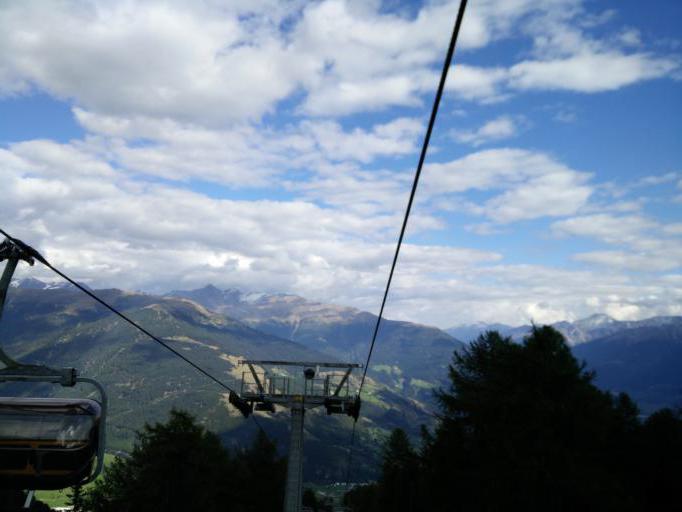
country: IT
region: Trentino-Alto Adige
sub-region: Bolzano
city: Malles Venosta
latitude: 46.7070
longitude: 10.4960
